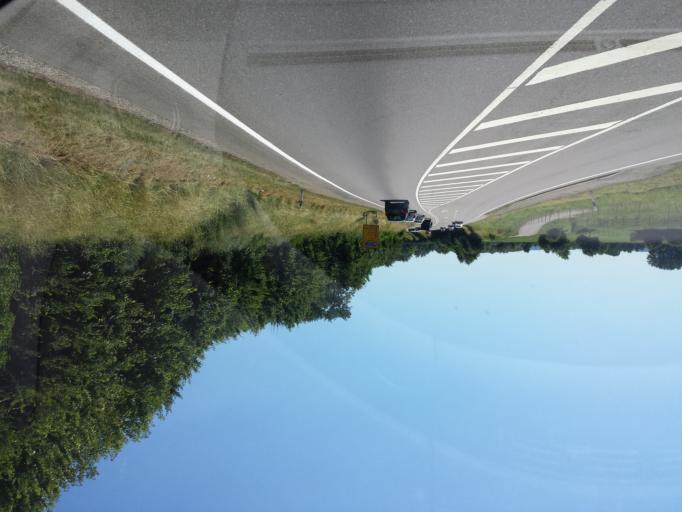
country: DE
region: Baden-Wuerttemberg
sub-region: Tuebingen Region
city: Owingen
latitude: 47.7928
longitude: 9.1527
